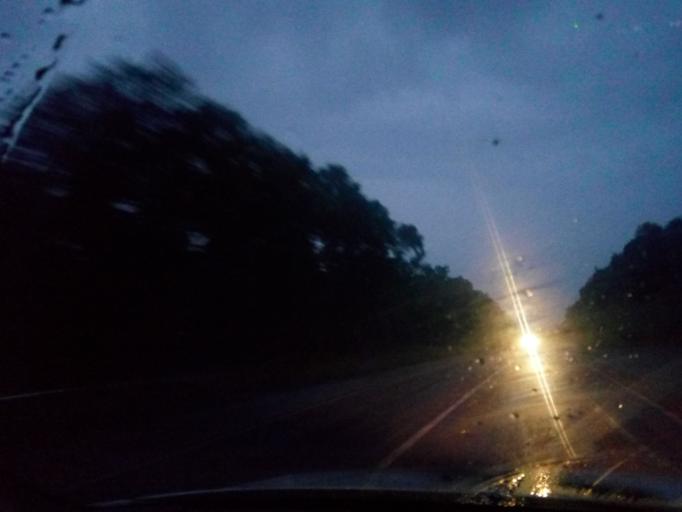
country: RU
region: Primorskiy
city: Dal'nerechensk
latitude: 45.8922
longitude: 133.7346
